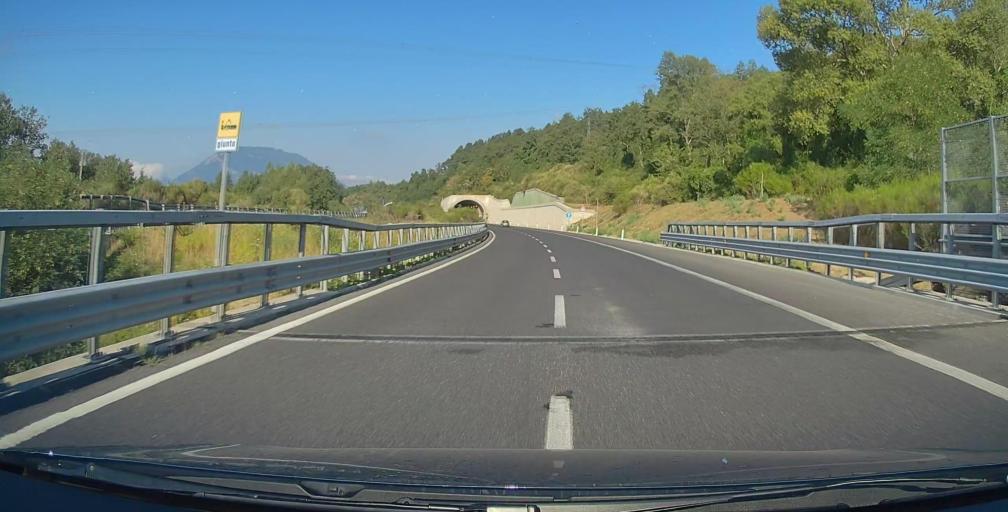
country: IT
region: Basilicate
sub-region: Provincia di Potenza
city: Nemoli
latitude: 40.0942
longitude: 15.8291
